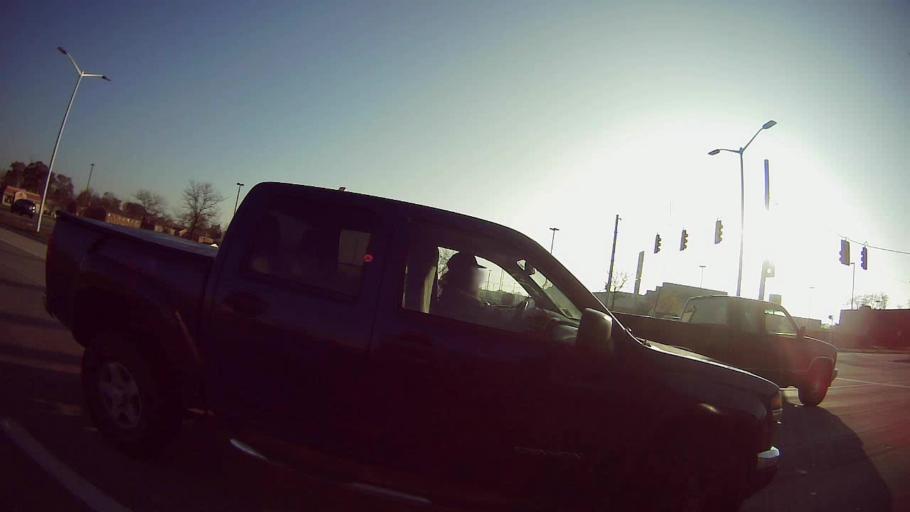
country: US
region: Michigan
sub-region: Oakland County
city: Oak Park
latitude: 42.4492
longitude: -83.2009
